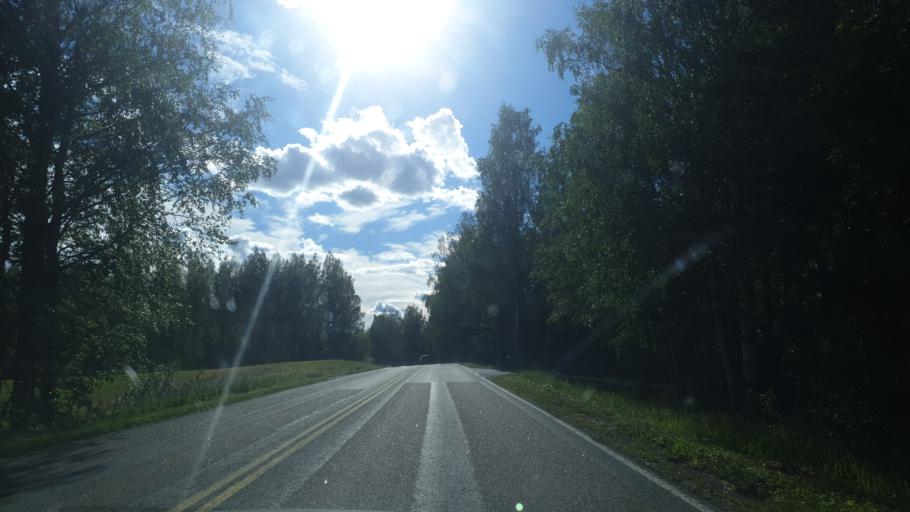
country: FI
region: Southern Savonia
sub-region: Mikkeli
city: Pertunmaa
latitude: 61.5233
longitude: 26.5125
